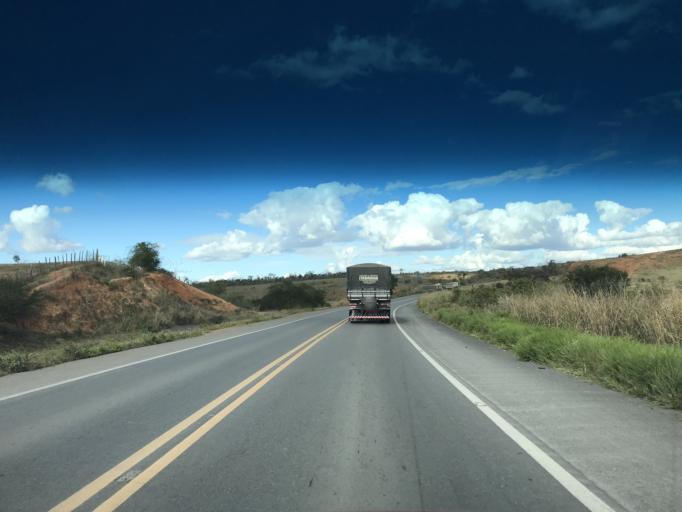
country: BR
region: Bahia
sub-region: Ruy Barbosa
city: Terra Nova
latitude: -12.4395
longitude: -40.8149
